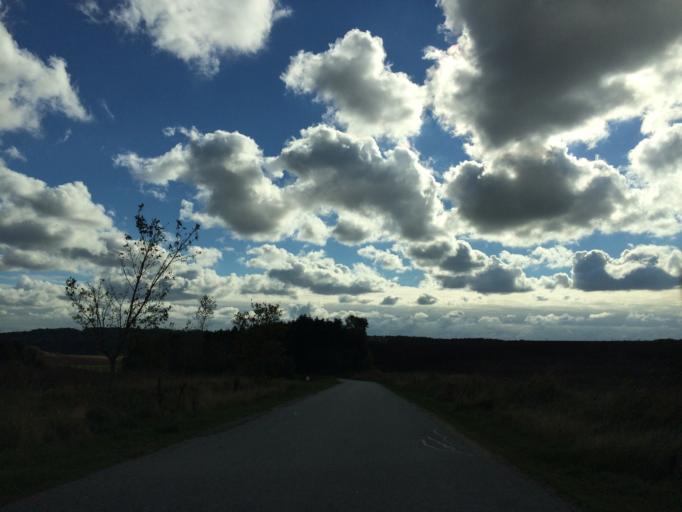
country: DK
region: Central Jutland
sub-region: Skanderborg Kommune
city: Ry
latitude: 56.1737
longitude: 9.7712
